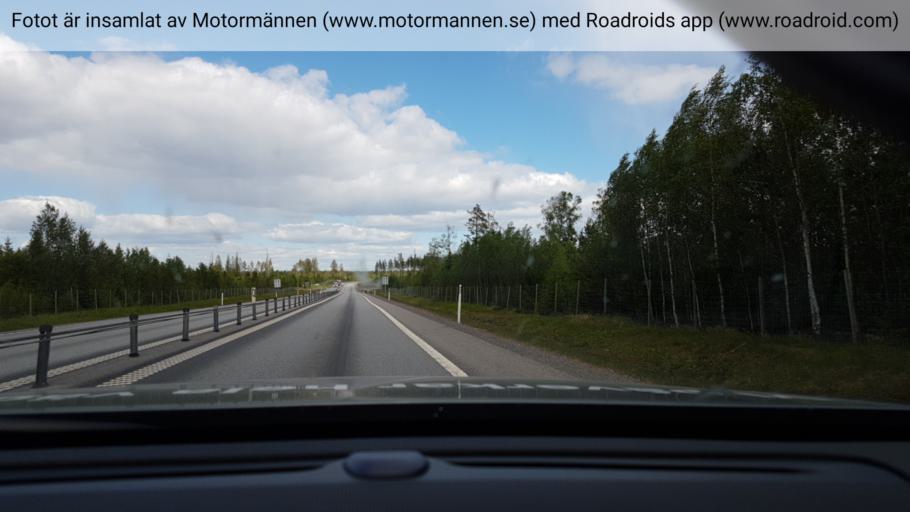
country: SE
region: Vaesterbotten
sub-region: Umea Kommun
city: Hoernefors
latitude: 63.6600
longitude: 19.9609
